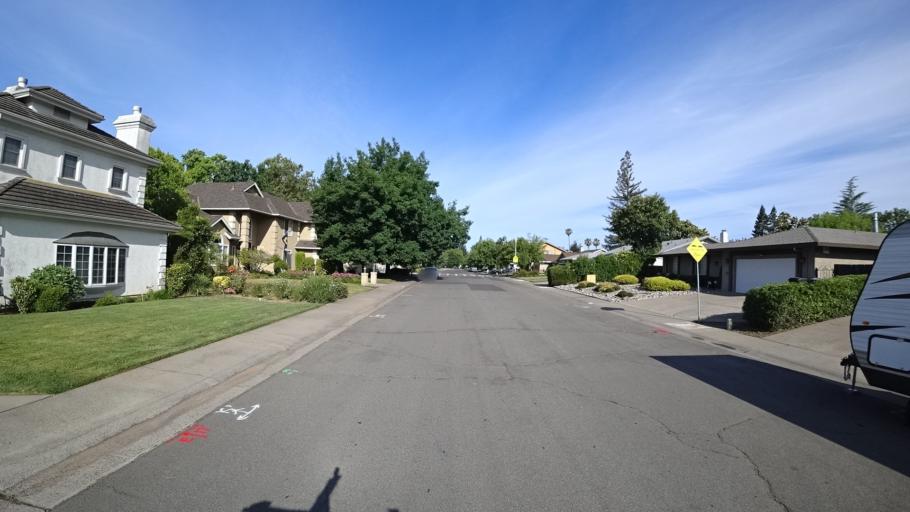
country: US
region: California
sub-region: Sacramento County
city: Rosemont
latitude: 38.5697
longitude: -121.3977
